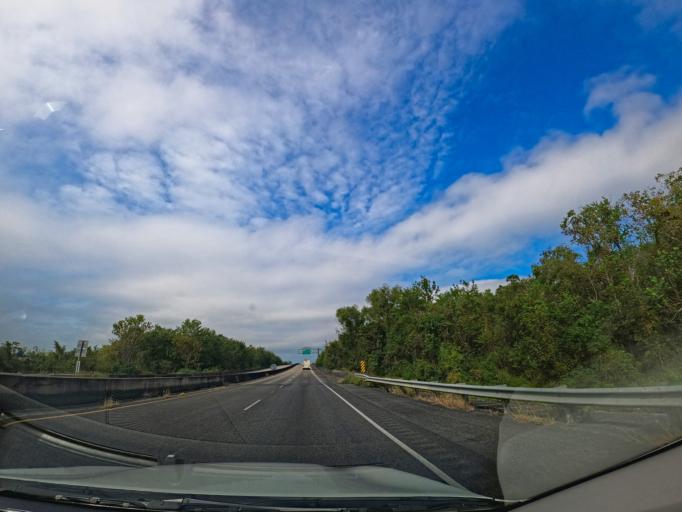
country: US
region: Louisiana
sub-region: Saint Mary Parish
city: Morgan City
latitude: 29.6970
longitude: -91.1694
